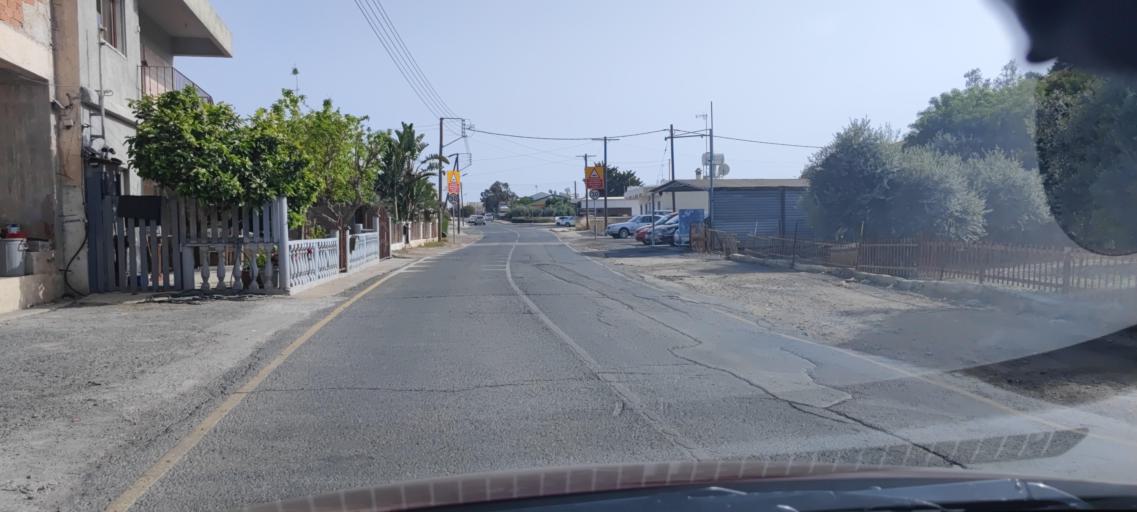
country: CY
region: Ammochostos
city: Deryneia
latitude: 35.0601
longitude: 33.9588
